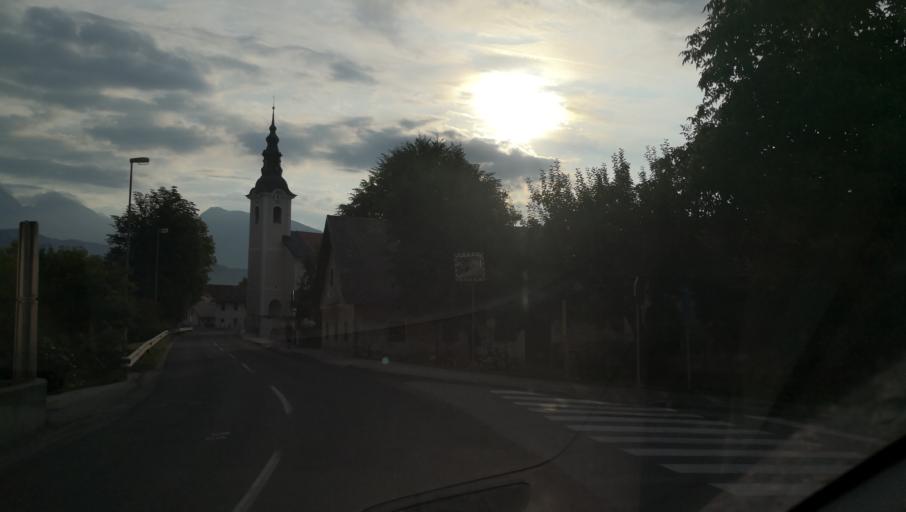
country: SI
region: Sencur
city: Sencur
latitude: 46.2699
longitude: 14.4150
